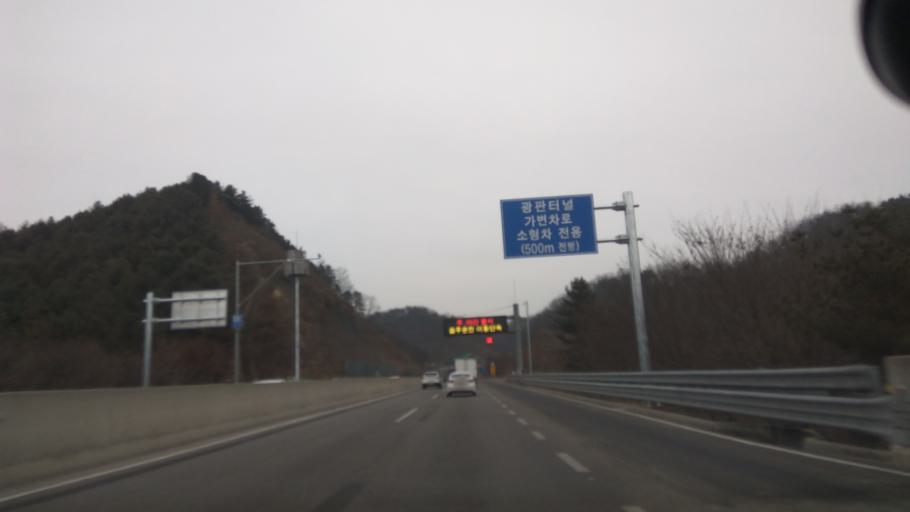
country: KR
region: Gangwon-do
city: Sindong
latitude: 37.7449
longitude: 127.6935
